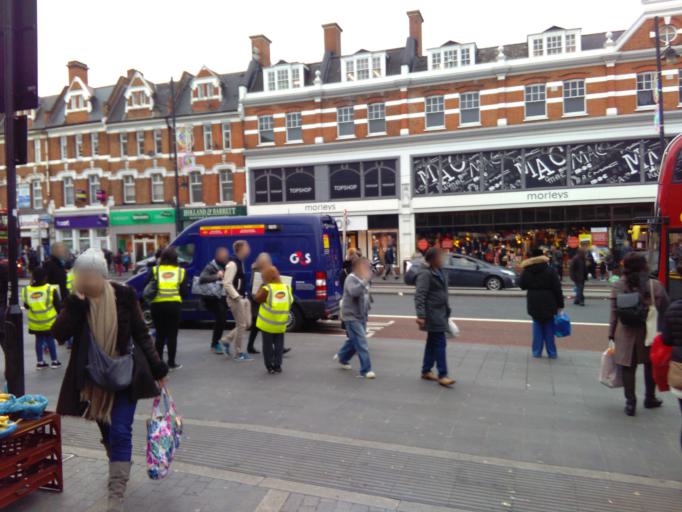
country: GB
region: England
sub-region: Greater London
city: Brixton
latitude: 51.4622
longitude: -0.1143
